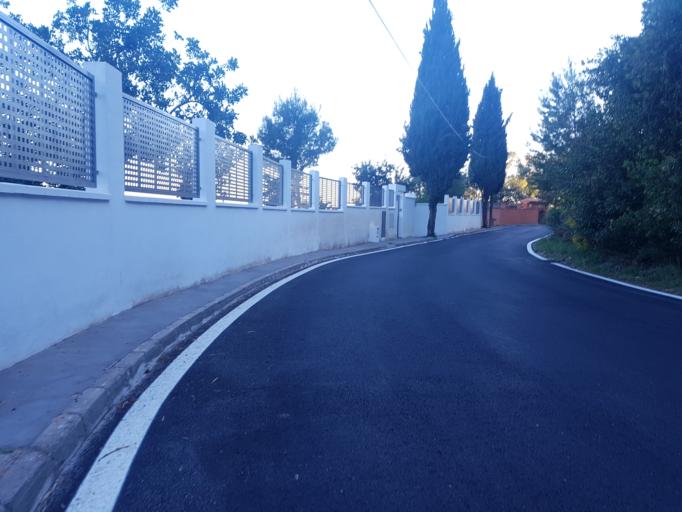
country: ES
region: Andalusia
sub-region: Provincia de Malaga
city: Marbella
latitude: 36.5285
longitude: -4.8854
